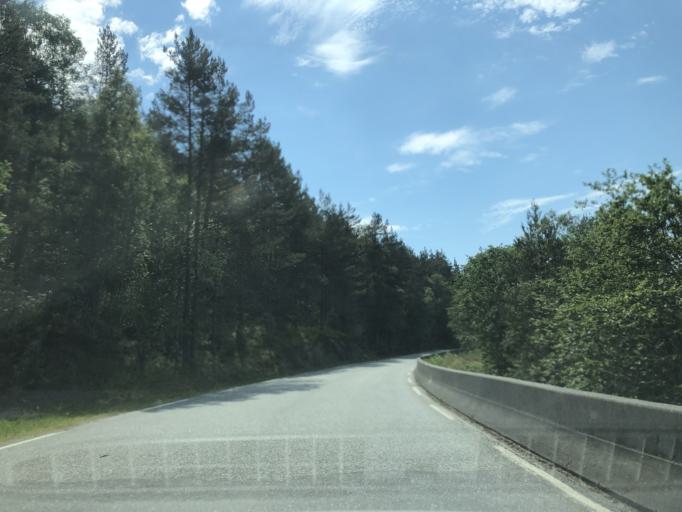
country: NO
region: Hordaland
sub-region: Jondal
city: Jondal
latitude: 60.2974
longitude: 6.2431
